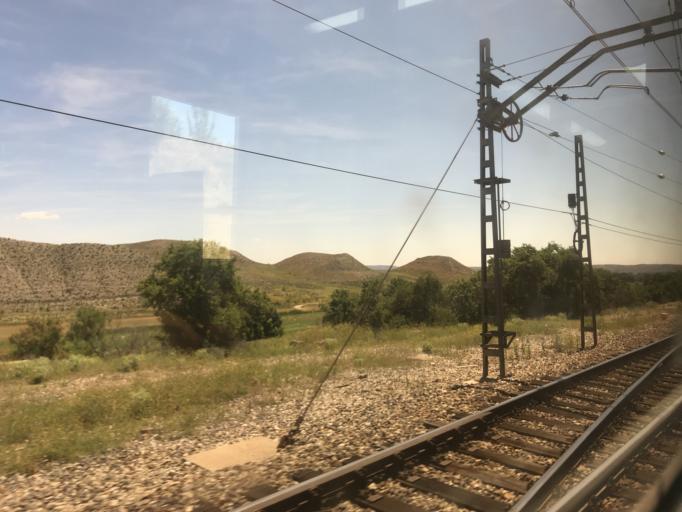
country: ES
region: Madrid
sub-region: Provincia de Madrid
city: Ciempozuelos
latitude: 40.1647
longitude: -3.6127
